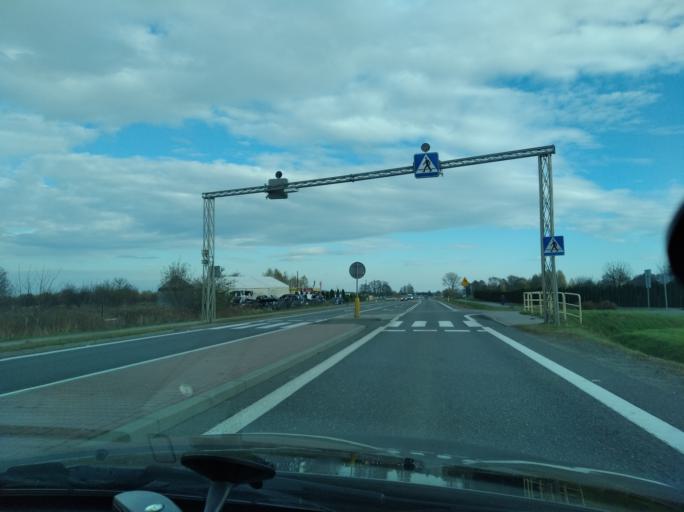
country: PL
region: Subcarpathian Voivodeship
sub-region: Powiat debicki
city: Debica
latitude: 50.0458
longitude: 21.4386
